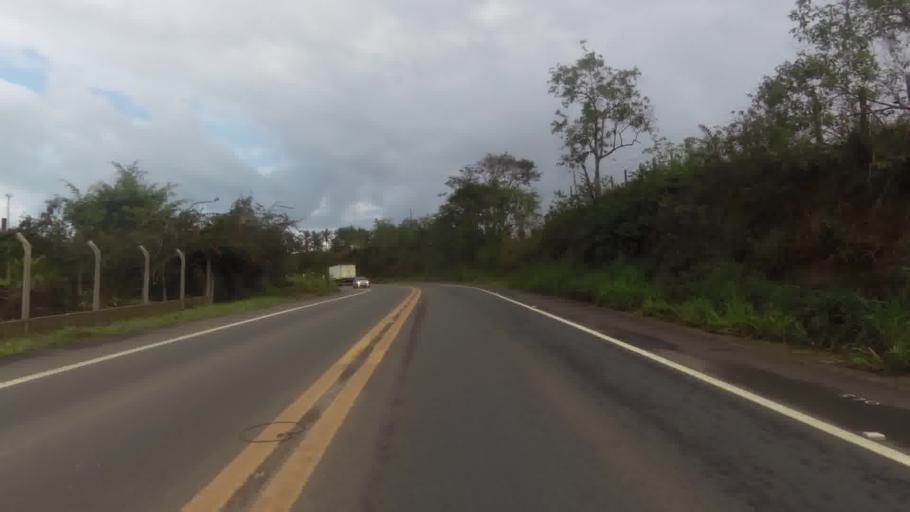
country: BR
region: Espirito Santo
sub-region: Piuma
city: Piuma
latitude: -20.8223
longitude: -40.6961
